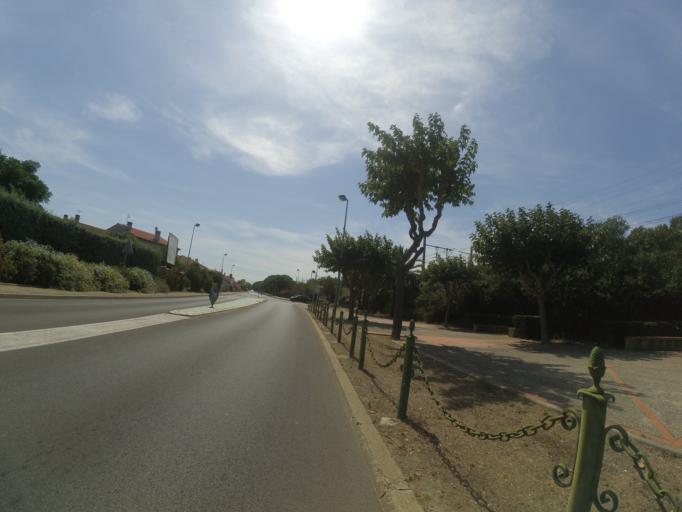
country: FR
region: Languedoc-Roussillon
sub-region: Departement des Pyrenees-Orientales
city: Rivesaltes
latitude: 42.7646
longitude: 2.8690
